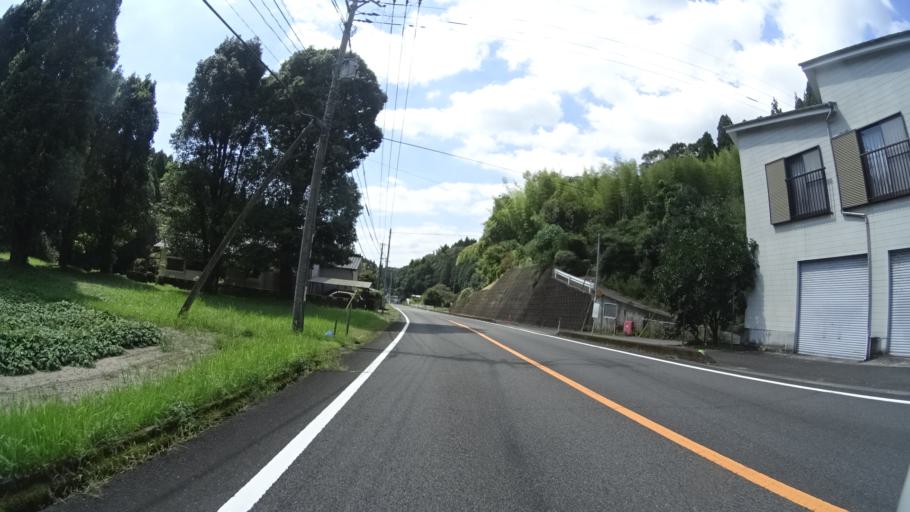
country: JP
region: Kagoshima
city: Kokubu-matsuki
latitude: 31.8571
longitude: 130.7678
